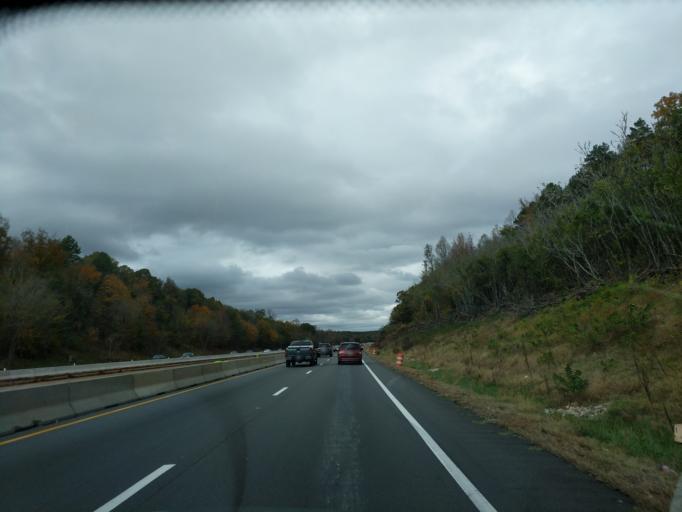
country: US
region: North Carolina
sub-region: Rowan County
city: Landis
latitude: 35.5168
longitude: -80.5692
